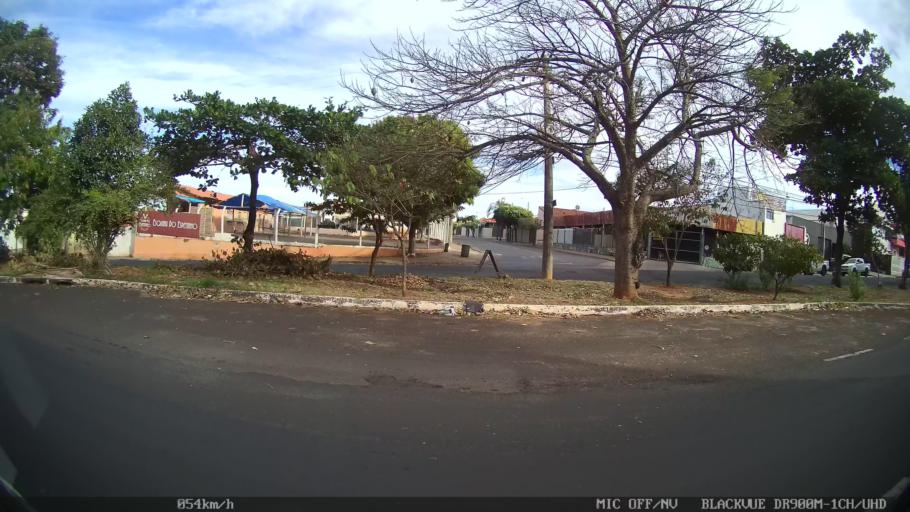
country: BR
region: Sao Paulo
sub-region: Catanduva
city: Catanduva
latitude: -21.1139
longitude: -48.9639
